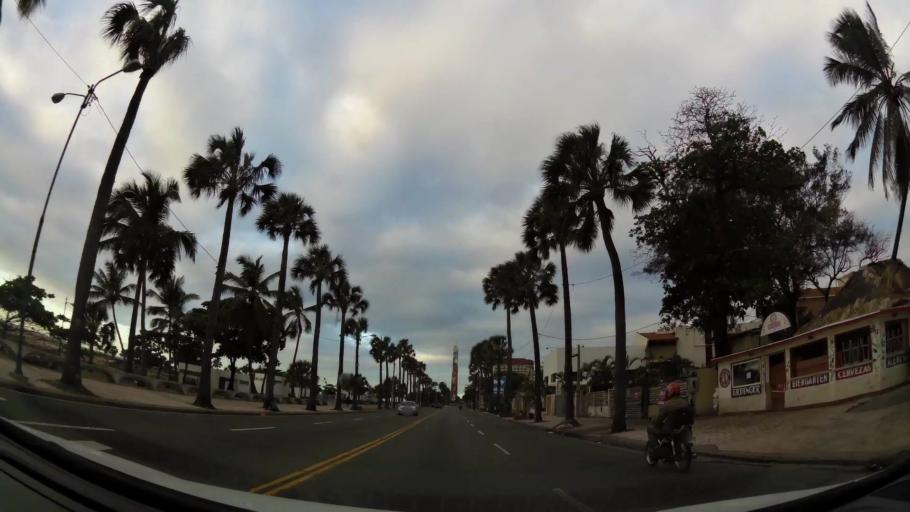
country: DO
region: Nacional
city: Ciudad Nueva
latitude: 18.4659
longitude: -69.8919
